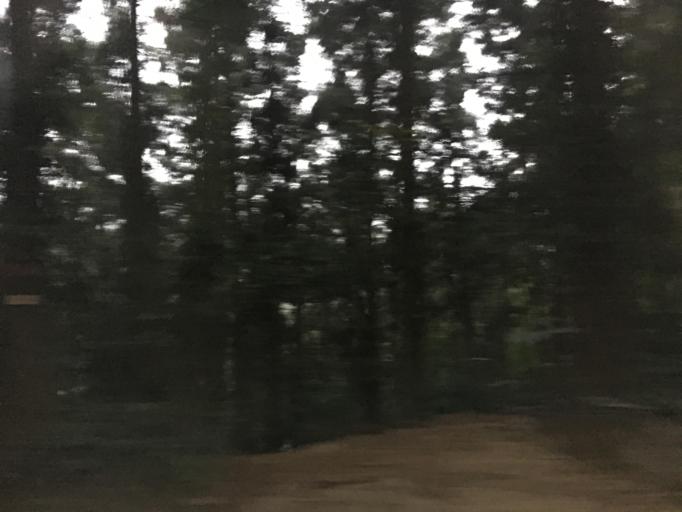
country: TW
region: Taiwan
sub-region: Chiayi
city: Jiayi Shi
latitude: 23.5071
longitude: 120.6601
